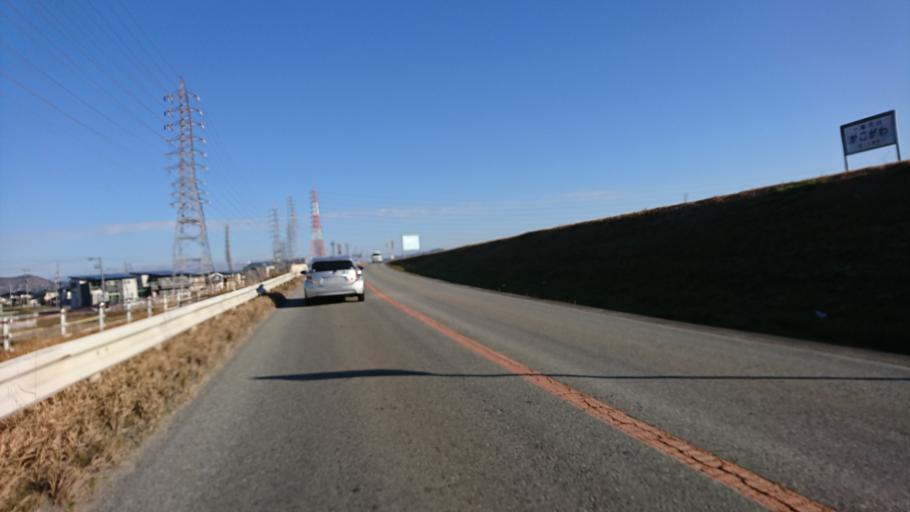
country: JP
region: Hyogo
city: Kakogawacho-honmachi
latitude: 34.7625
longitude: 134.8055
